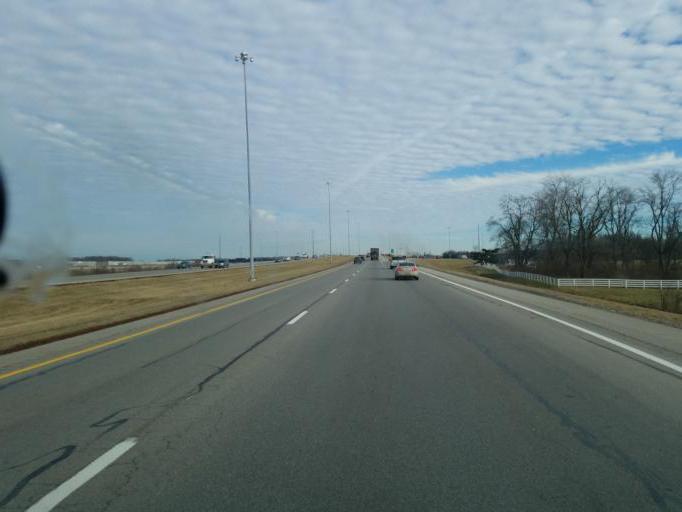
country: US
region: Ohio
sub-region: Franklin County
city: New Albany
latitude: 40.0795
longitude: -82.7610
